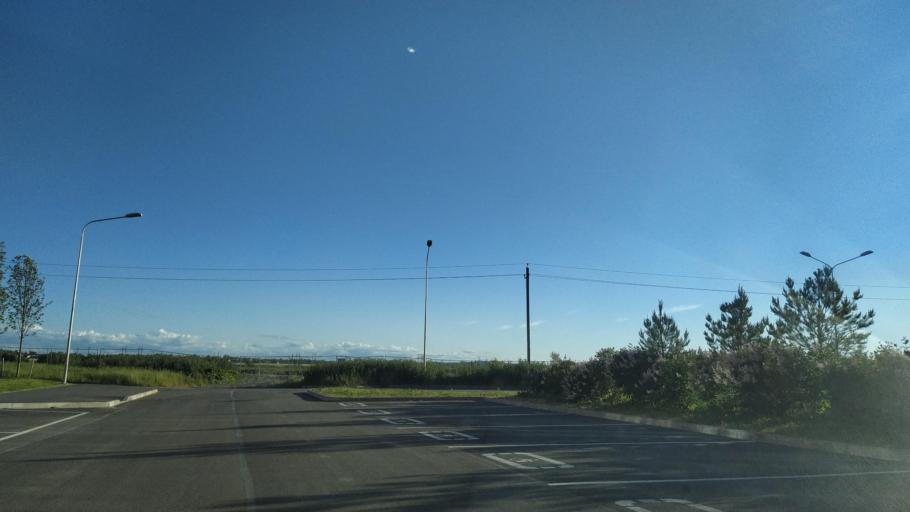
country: RU
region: St.-Petersburg
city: Aleksandrovskaya
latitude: 59.7545
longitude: 30.3582
